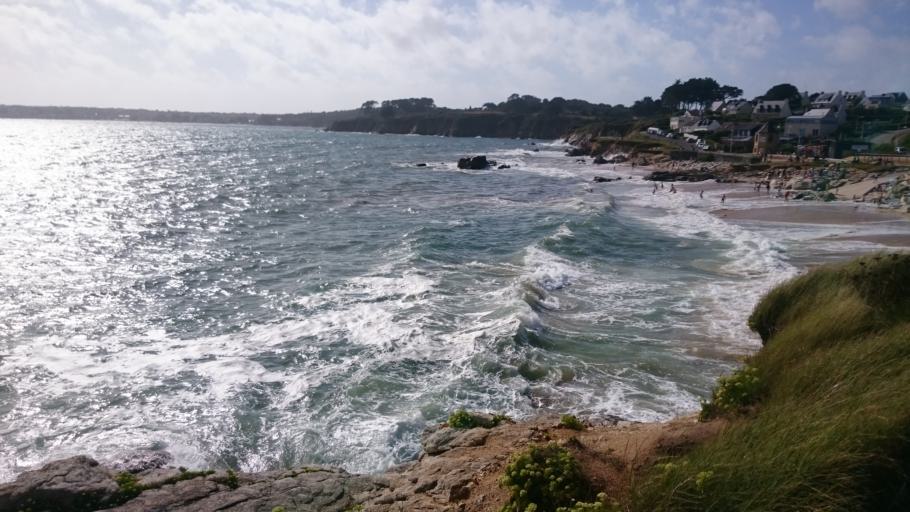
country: FR
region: Brittany
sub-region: Departement du Finistere
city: Plougonvelin
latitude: 48.3539
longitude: -4.6723
